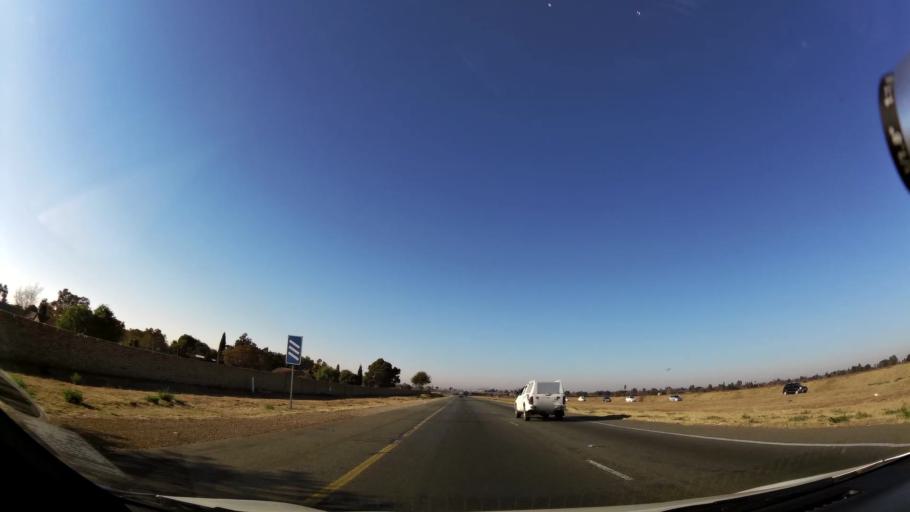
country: ZA
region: Gauteng
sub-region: Ekurhuleni Metropolitan Municipality
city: Germiston
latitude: -26.2985
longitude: 28.1082
